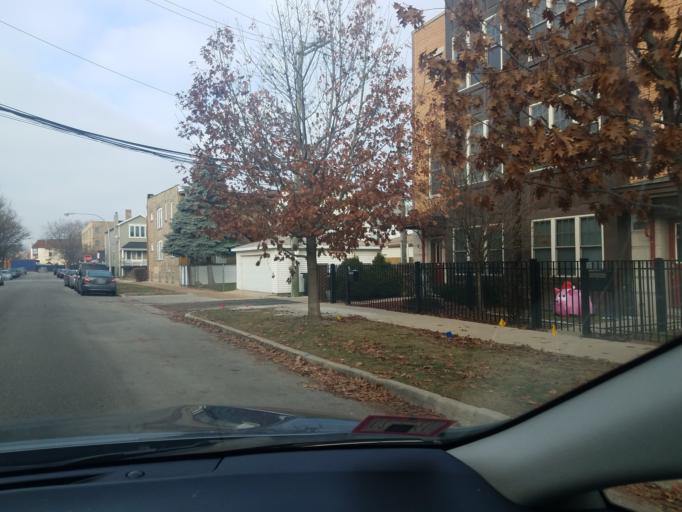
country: US
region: Illinois
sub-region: Cook County
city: Lincolnwood
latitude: 41.9448
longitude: -87.7033
